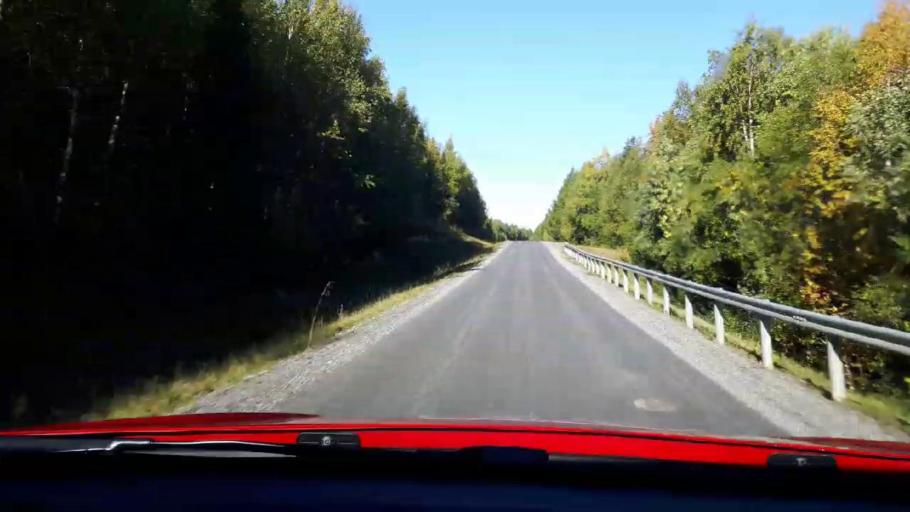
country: NO
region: Nord-Trondelag
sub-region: Lierne
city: Sandvika
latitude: 64.5355
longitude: 14.0188
